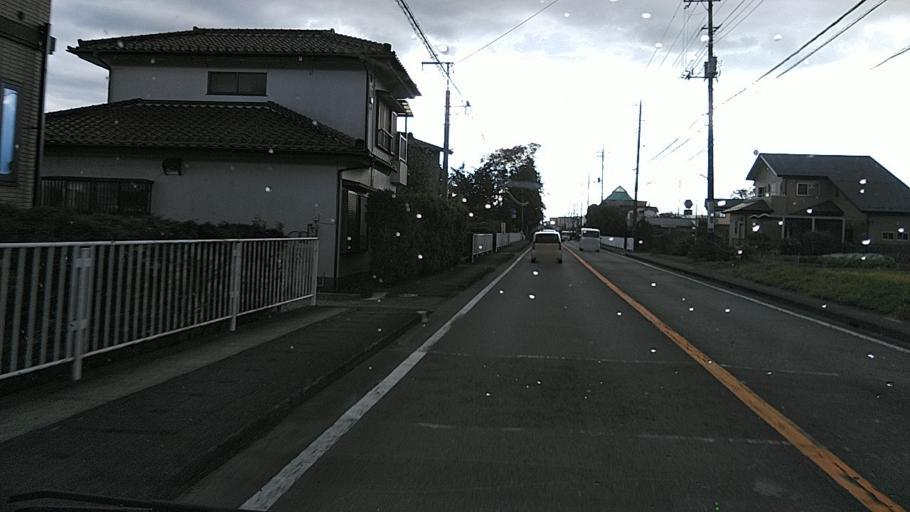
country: JP
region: Shizuoka
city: Gotemba
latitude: 35.3236
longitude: 138.9434
